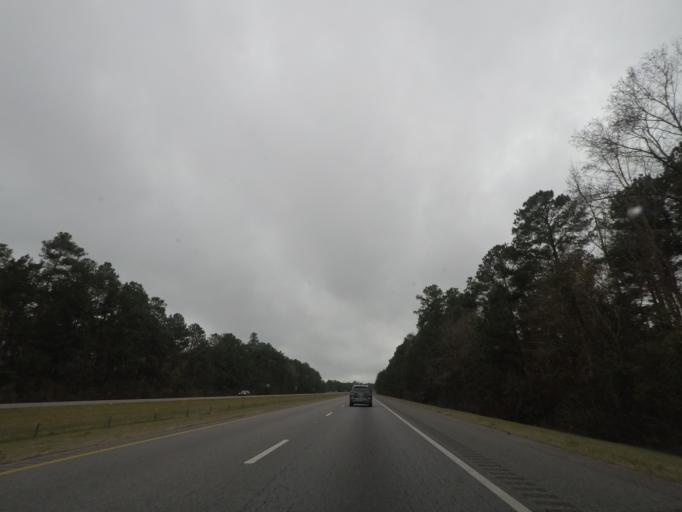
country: US
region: South Carolina
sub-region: Orangeburg County
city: Holly Hill
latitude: 33.4233
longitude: -80.4919
